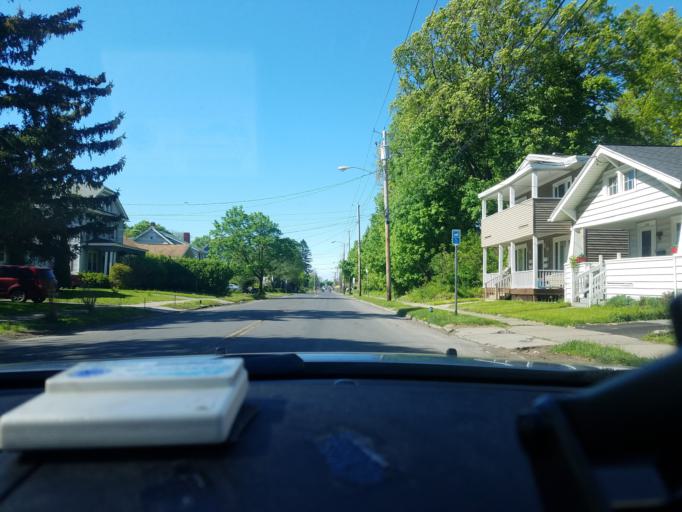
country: US
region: New York
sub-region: Onondaga County
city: Lyncourt
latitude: 43.0668
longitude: -76.1228
